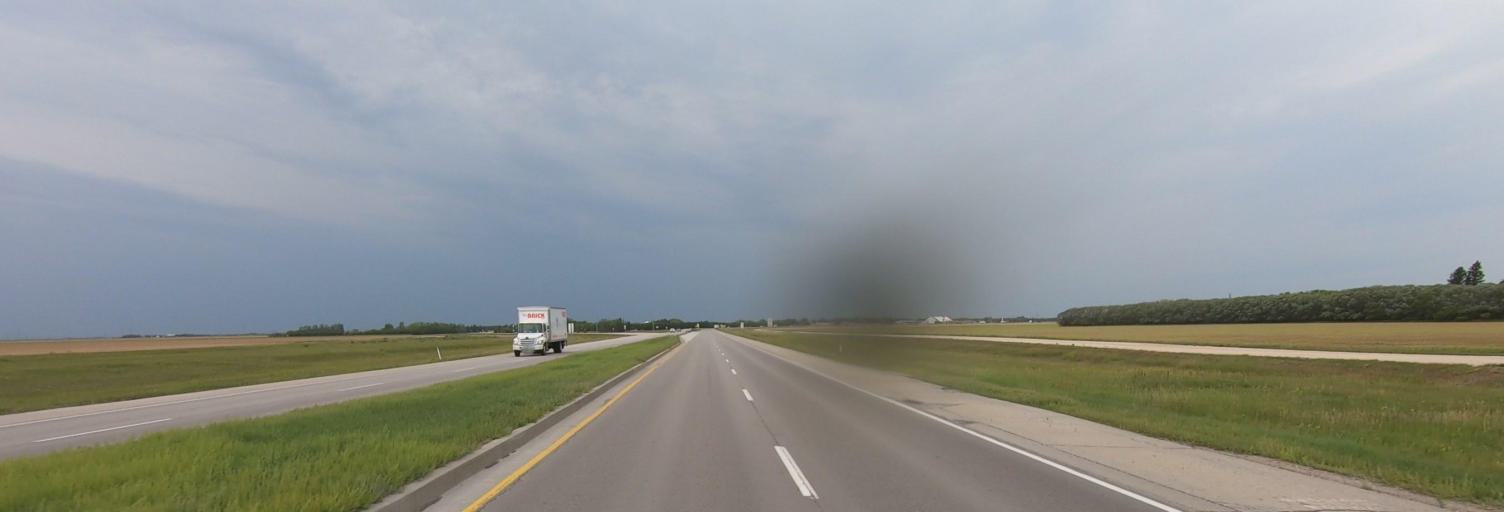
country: CA
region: Manitoba
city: Headingley
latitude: 49.7691
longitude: -97.2994
